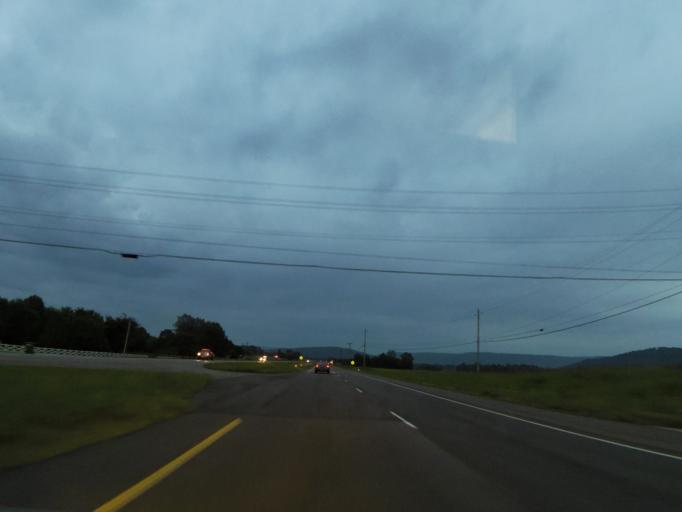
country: US
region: Alabama
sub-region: Madison County
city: Moores Mill
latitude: 34.7396
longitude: -86.4390
